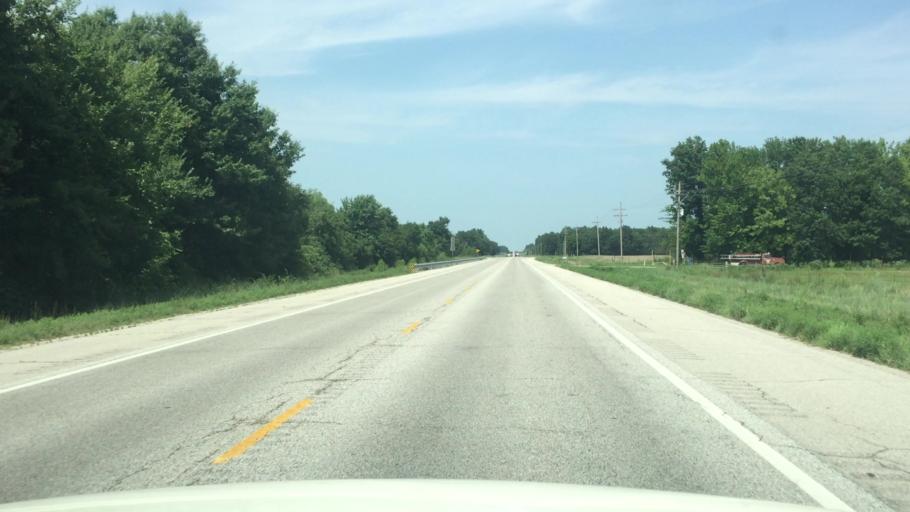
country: US
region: Kansas
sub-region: Cherokee County
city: Galena
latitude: 37.1304
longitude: -94.7043
